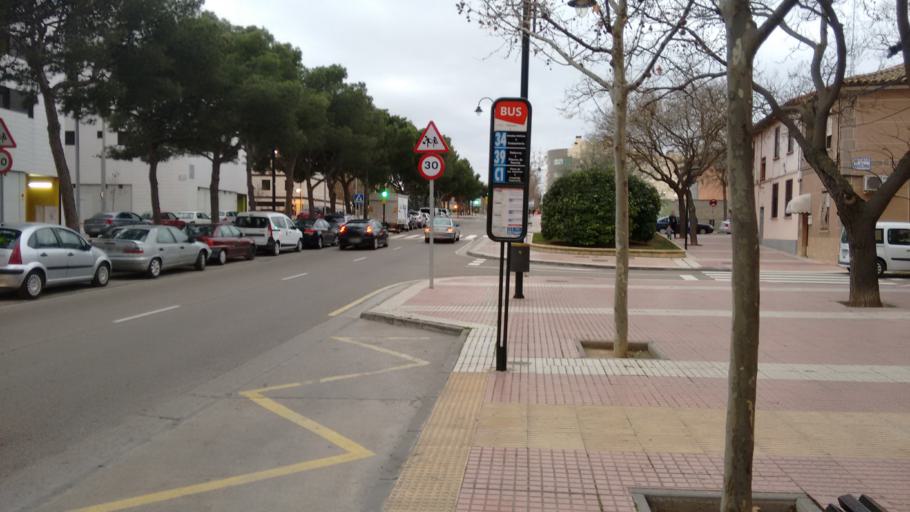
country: ES
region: Aragon
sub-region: Provincia de Zaragoza
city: Delicias
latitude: 41.6276
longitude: -0.8882
